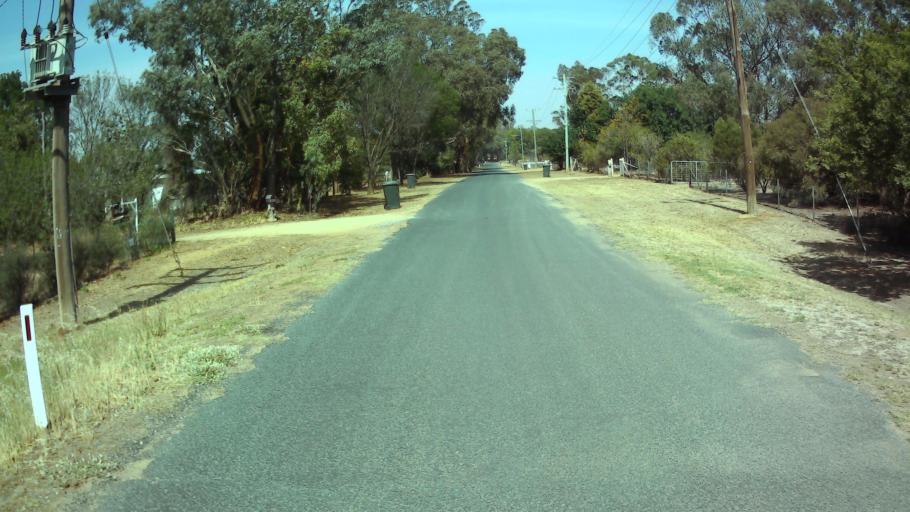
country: AU
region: New South Wales
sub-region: Weddin
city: Grenfell
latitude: -33.8952
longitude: 148.1497
